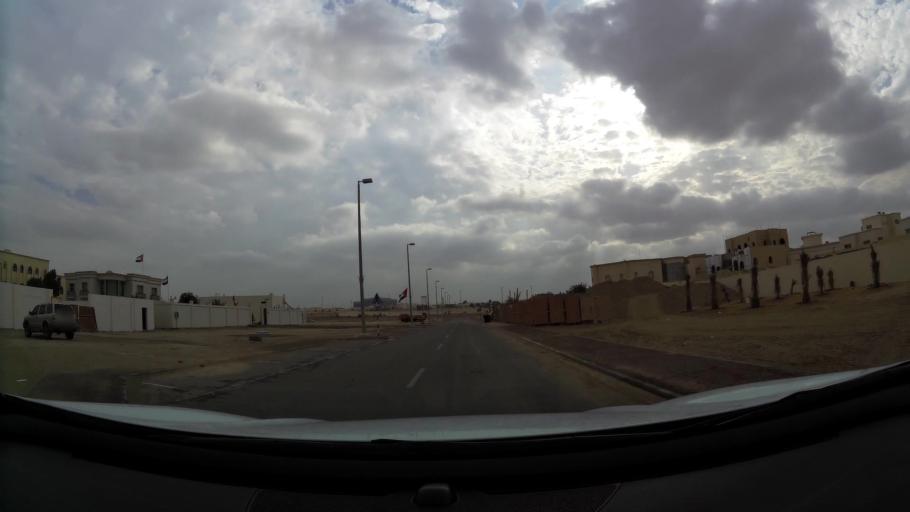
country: AE
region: Abu Dhabi
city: Abu Dhabi
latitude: 24.3401
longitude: 54.6215
